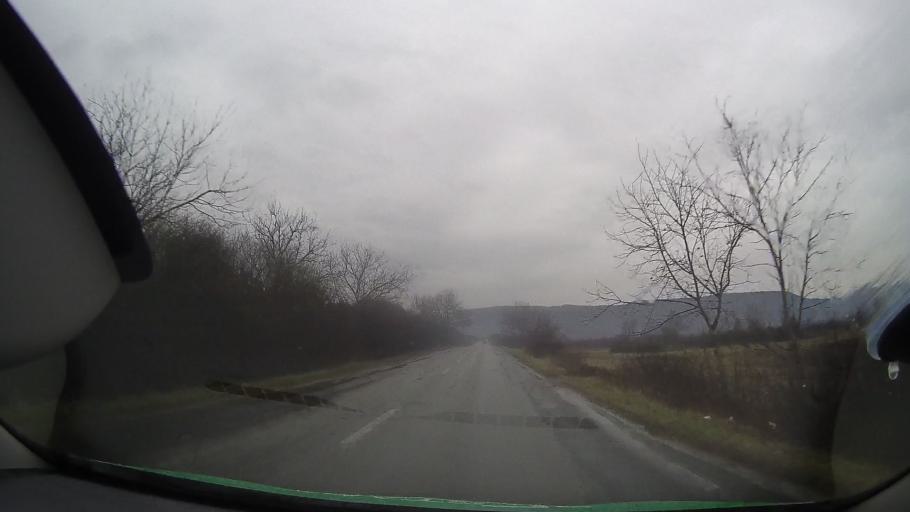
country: RO
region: Bihor
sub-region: Comuna Sambata
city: Sambata
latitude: 46.7799
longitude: 22.1876
